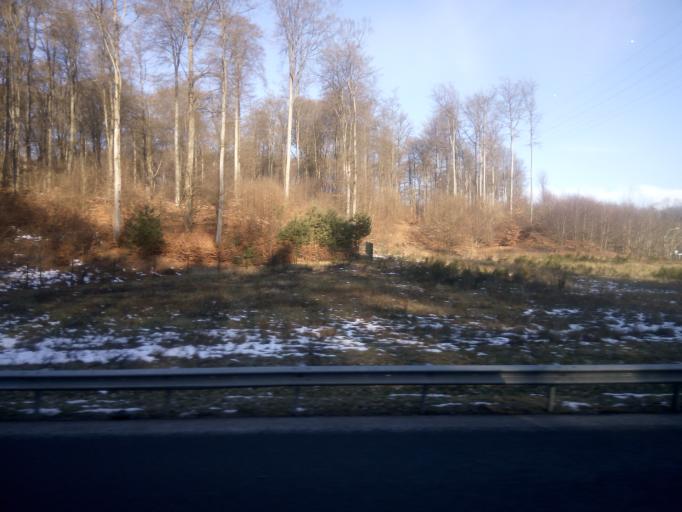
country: LU
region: Luxembourg
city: Helmsange
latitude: 49.6509
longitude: 6.1830
